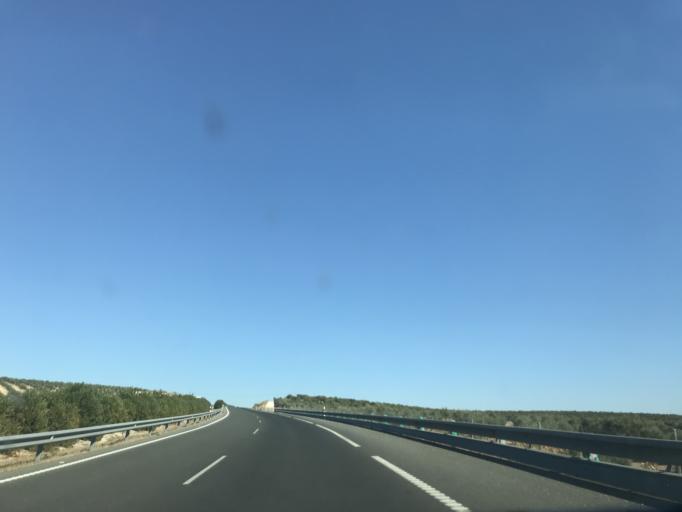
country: ES
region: Andalusia
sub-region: Provincia de Sevilla
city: La Puebla de Cazalla
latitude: 37.2310
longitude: -5.2415
